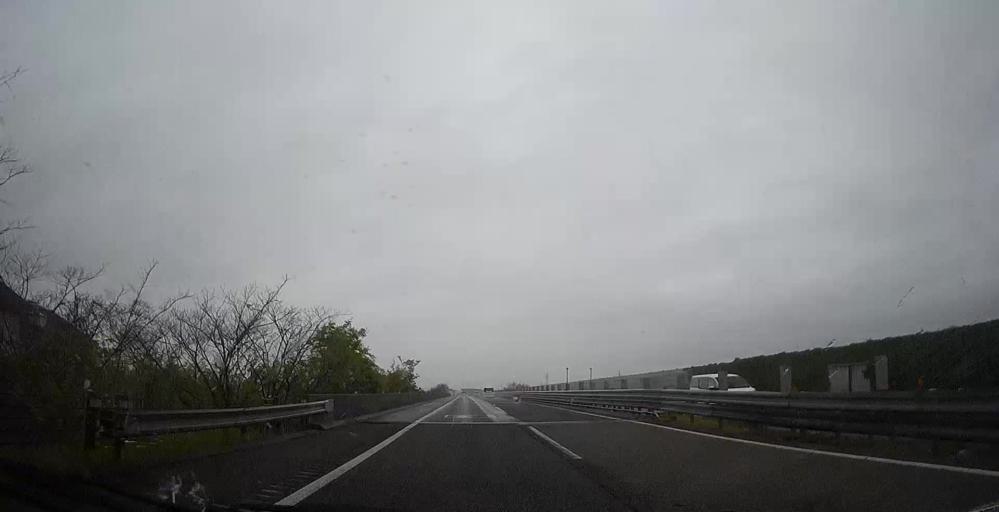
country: JP
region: Niigata
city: Sanjo
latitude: 37.6140
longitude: 138.9180
